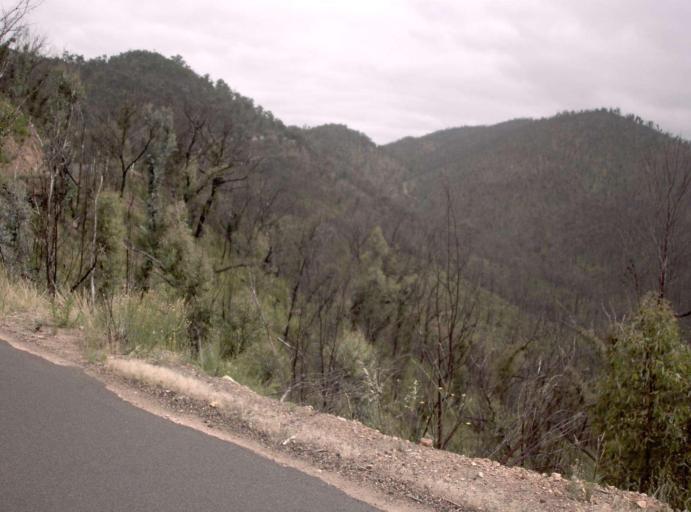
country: AU
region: Victoria
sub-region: Wellington
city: Heyfield
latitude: -37.7290
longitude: 146.6700
